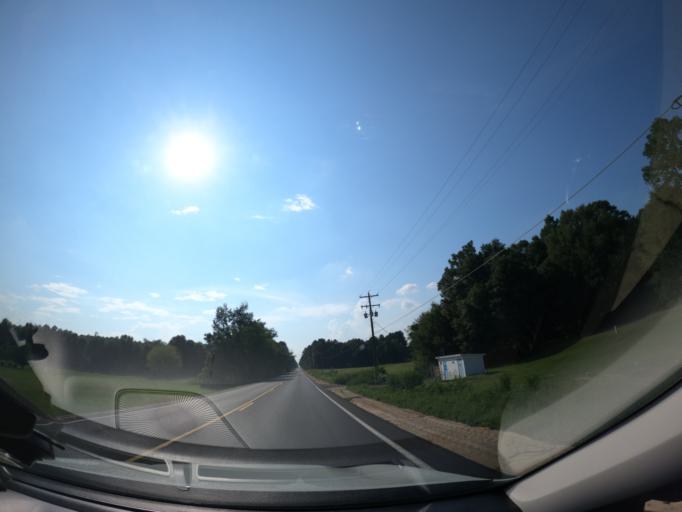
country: US
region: South Carolina
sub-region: Aiken County
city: New Ellenton
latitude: 33.3974
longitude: -81.7498
